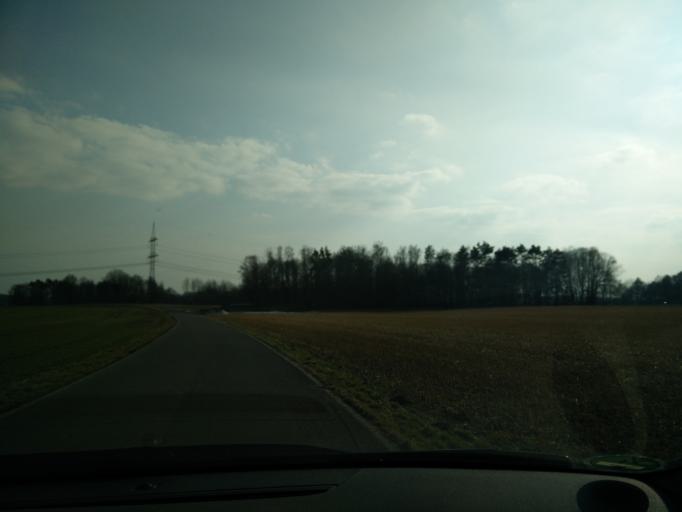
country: DE
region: Saxony
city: Konigsfeld
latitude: 51.1022
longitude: 12.7343
